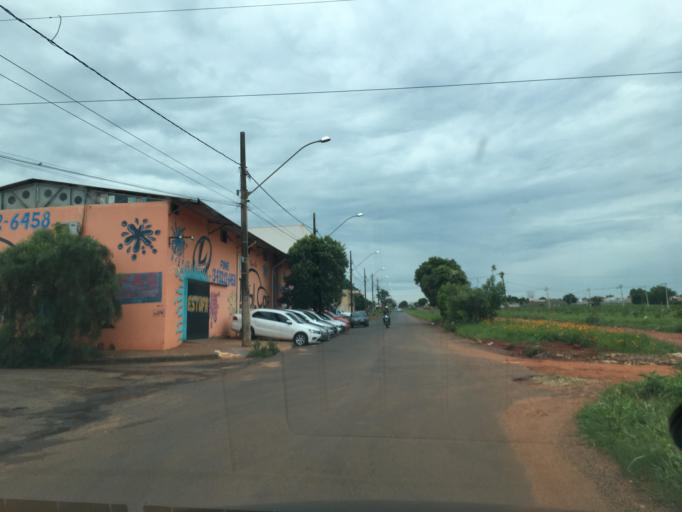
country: BR
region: Minas Gerais
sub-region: Uberlandia
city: Uberlandia
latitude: -18.8648
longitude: -48.2227
